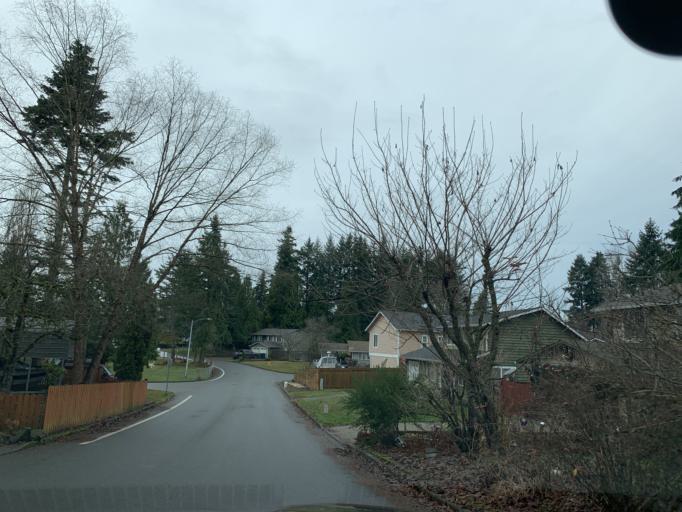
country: US
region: Washington
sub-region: King County
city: Woodinville
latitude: 47.7419
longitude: -122.1715
